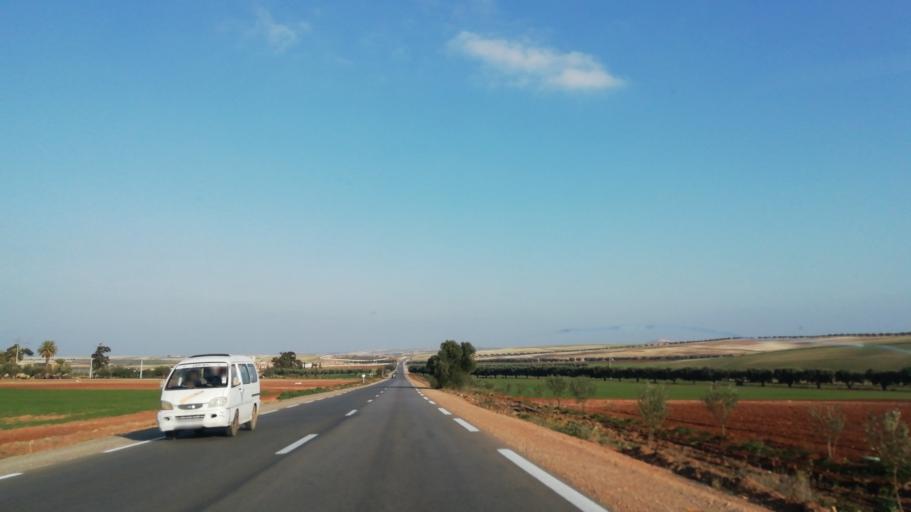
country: DZ
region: Sidi Bel Abbes
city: Sidi Bel Abbes
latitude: 35.1748
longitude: -0.8251
